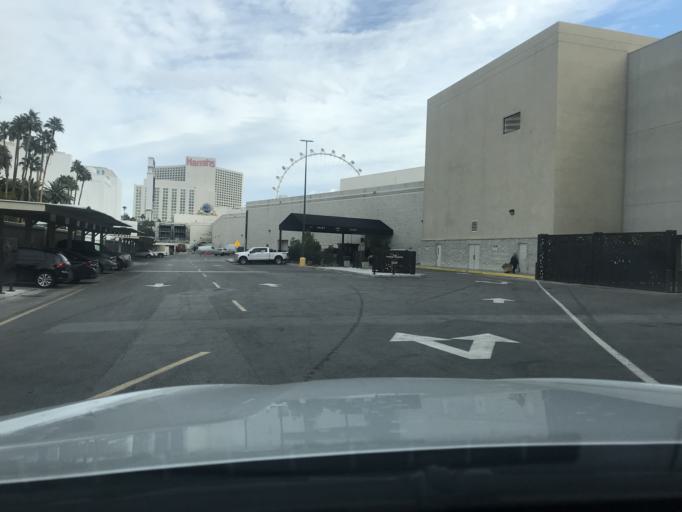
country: US
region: Nevada
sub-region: Clark County
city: Paradise
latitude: 36.1197
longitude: -115.1774
